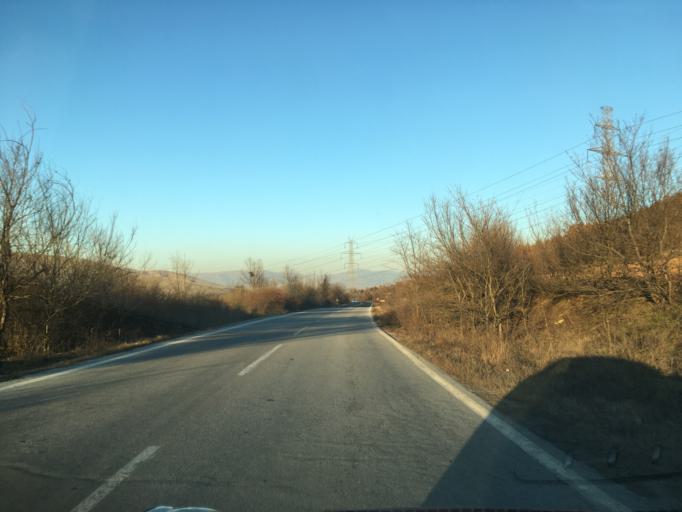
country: GR
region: West Macedonia
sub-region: Nomos Kozanis
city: Koila
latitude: 40.3181
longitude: 21.7638
